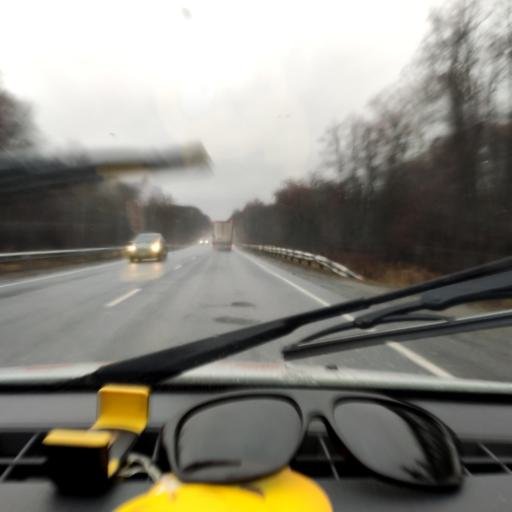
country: RU
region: Bashkortostan
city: Iglino
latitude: 54.7677
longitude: 56.4351
